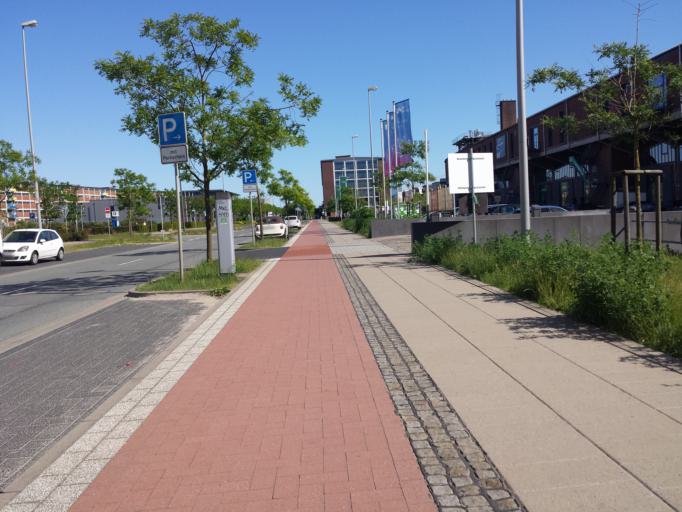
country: DE
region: Bremen
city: Bremen
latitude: 53.0910
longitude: 8.7746
